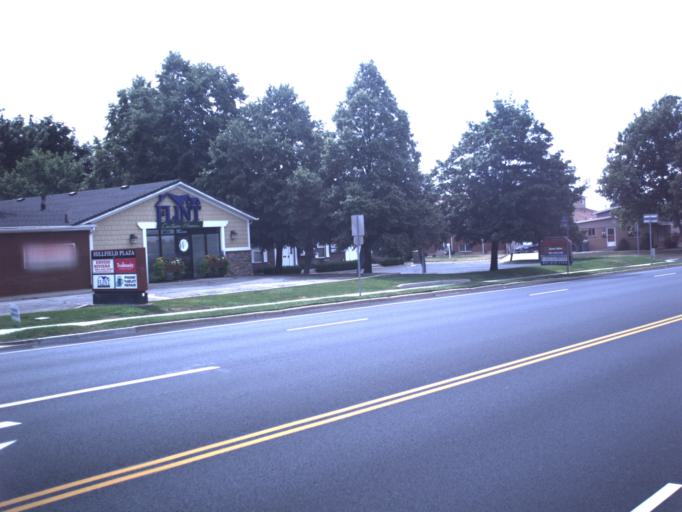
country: US
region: Utah
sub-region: Davis County
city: Layton
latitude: 41.0804
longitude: -111.9736
